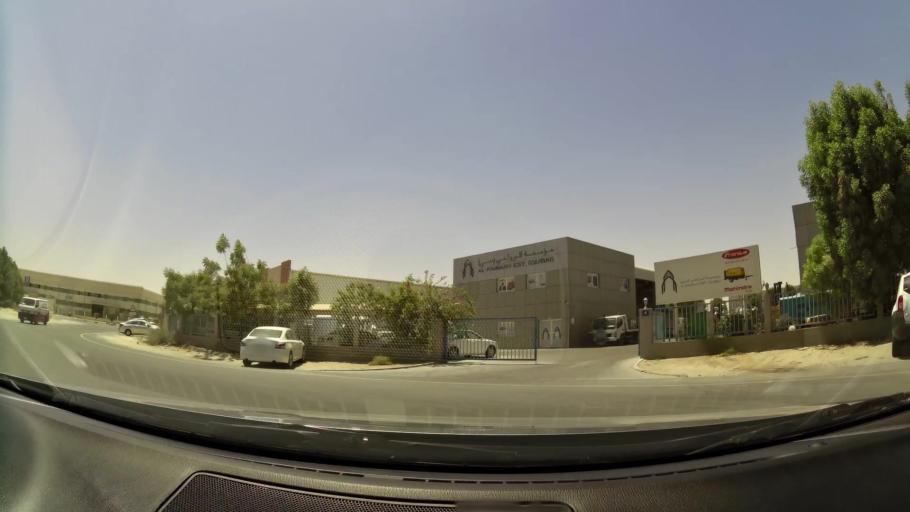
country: AE
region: Dubai
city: Dubai
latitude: 24.9673
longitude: 55.2039
